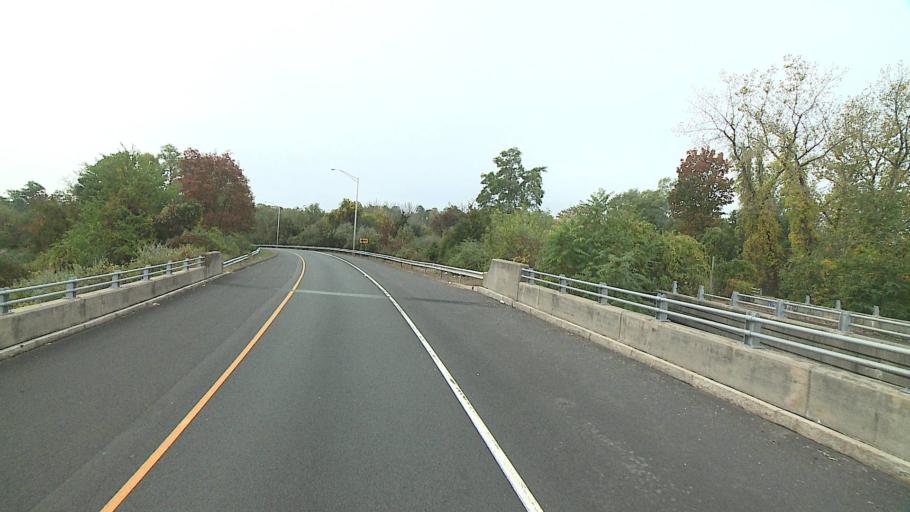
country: US
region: Connecticut
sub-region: Hartford County
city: West Hartford
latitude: 41.7267
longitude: -72.7724
